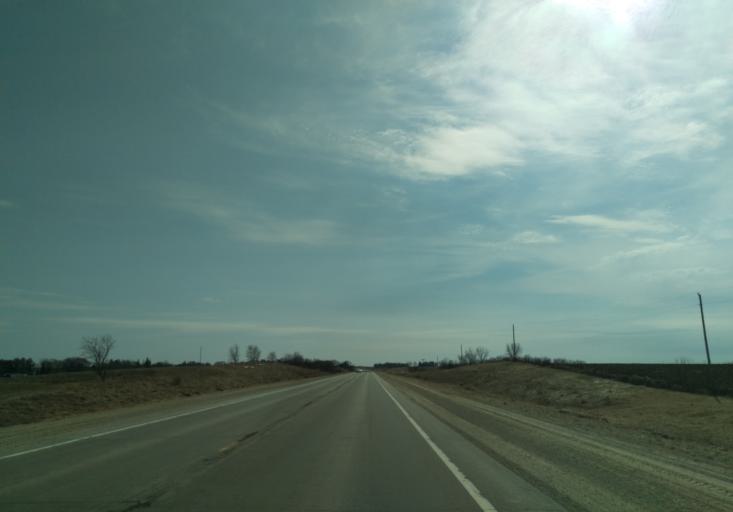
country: US
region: Minnesota
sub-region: Fillmore County
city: Harmony
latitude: 43.4685
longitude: -91.8699
